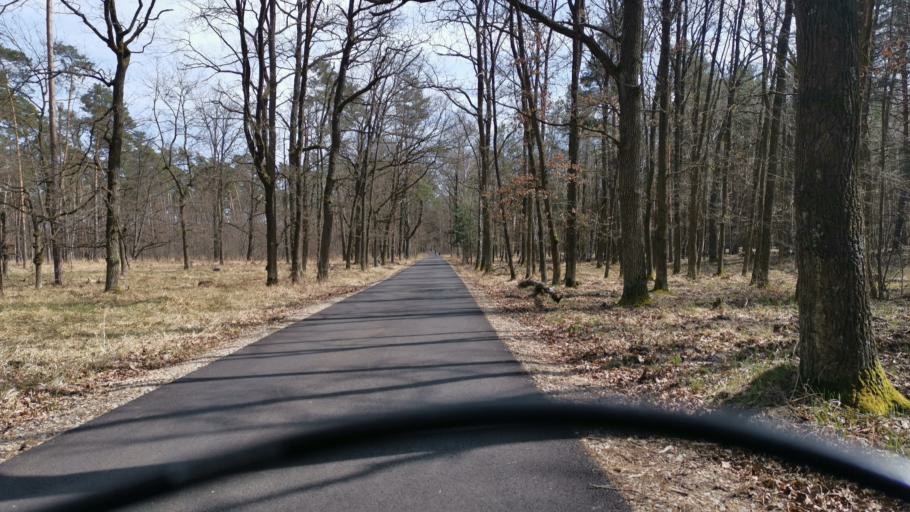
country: SK
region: Trnavsky
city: Gbely
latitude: 48.7118
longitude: 17.0623
